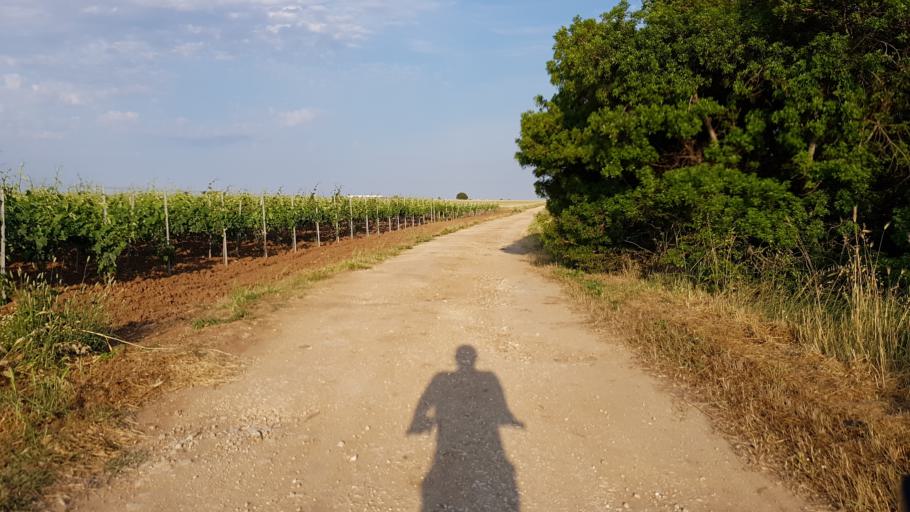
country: IT
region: Apulia
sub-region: Provincia di Brindisi
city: Brindisi
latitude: 40.6266
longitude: 17.8712
